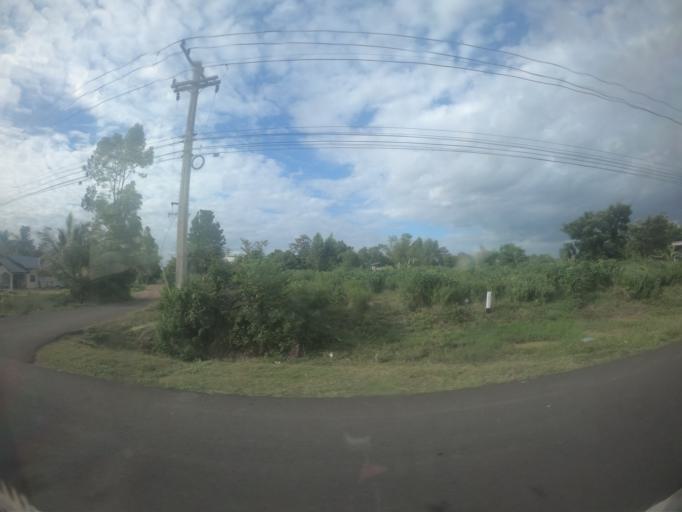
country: TH
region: Surin
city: Prasat
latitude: 14.6028
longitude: 103.4304
